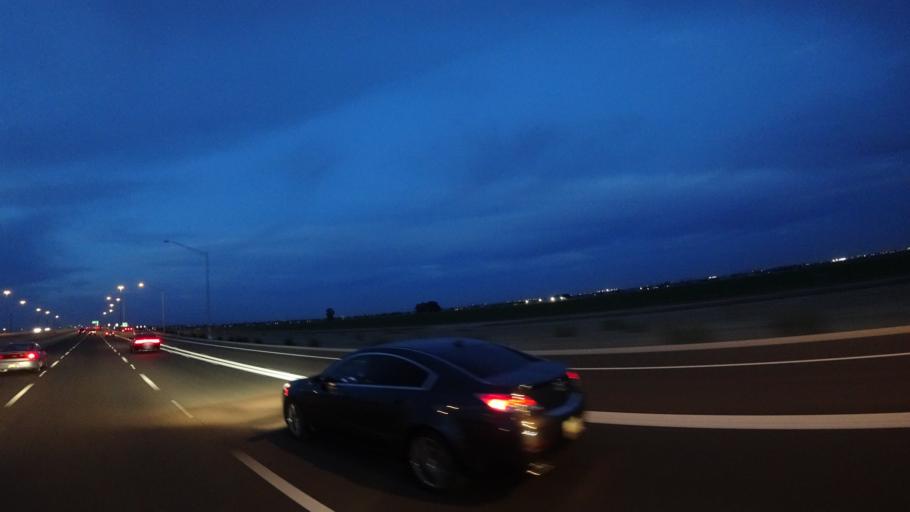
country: US
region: Arizona
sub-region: Maricopa County
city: Citrus Park
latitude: 33.5749
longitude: -112.4180
